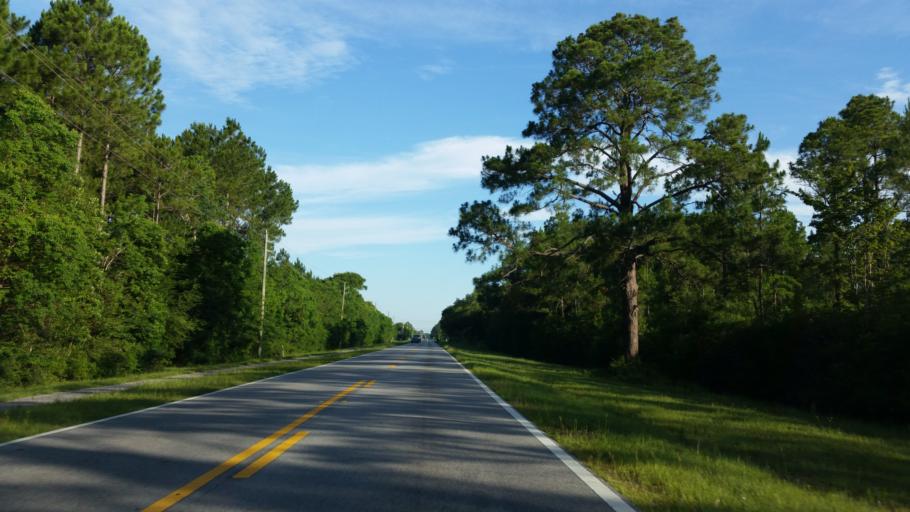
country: US
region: Florida
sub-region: Escambia County
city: Myrtle Grove
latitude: 30.3836
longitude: -87.3532
